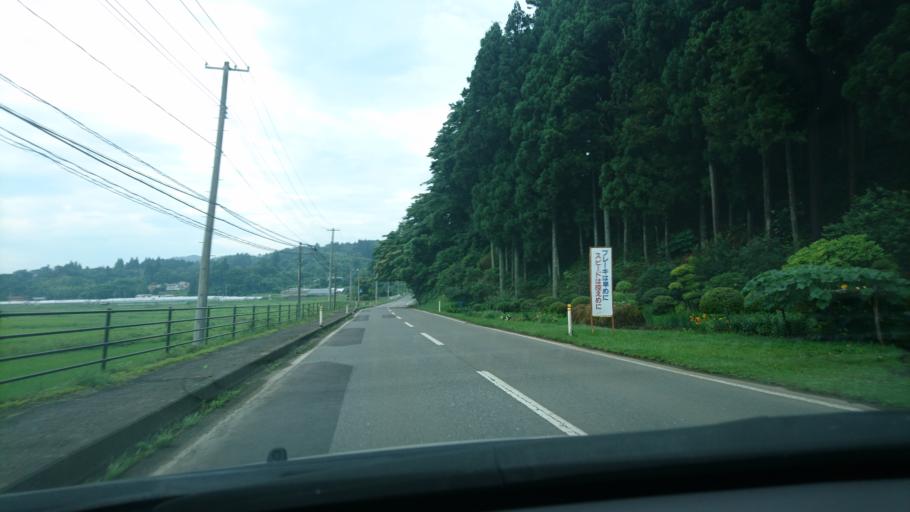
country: JP
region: Iwate
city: Ichinoseki
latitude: 38.9306
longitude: 141.4226
